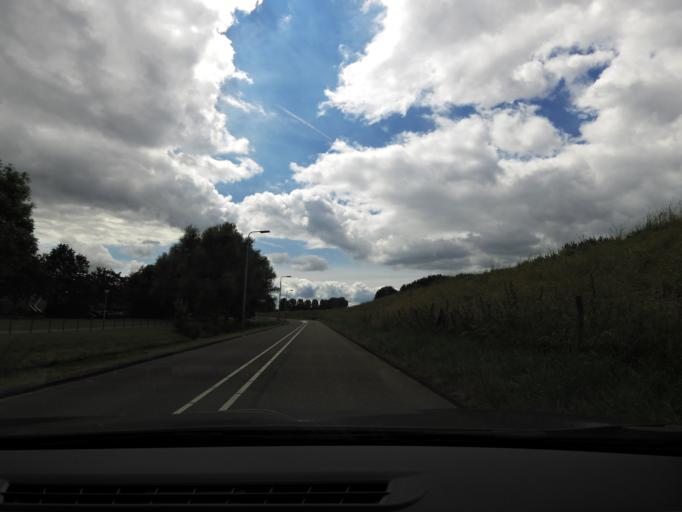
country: NL
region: South Holland
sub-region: Gemeente Oud-Beijerland
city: Oud-Beijerland
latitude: 51.8267
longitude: 4.3920
